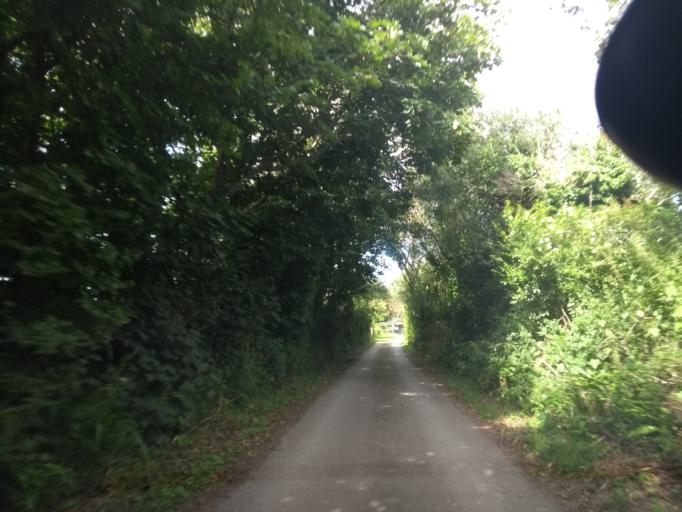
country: GB
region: England
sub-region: Devon
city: Modbury
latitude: 50.2952
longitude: -3.8962
